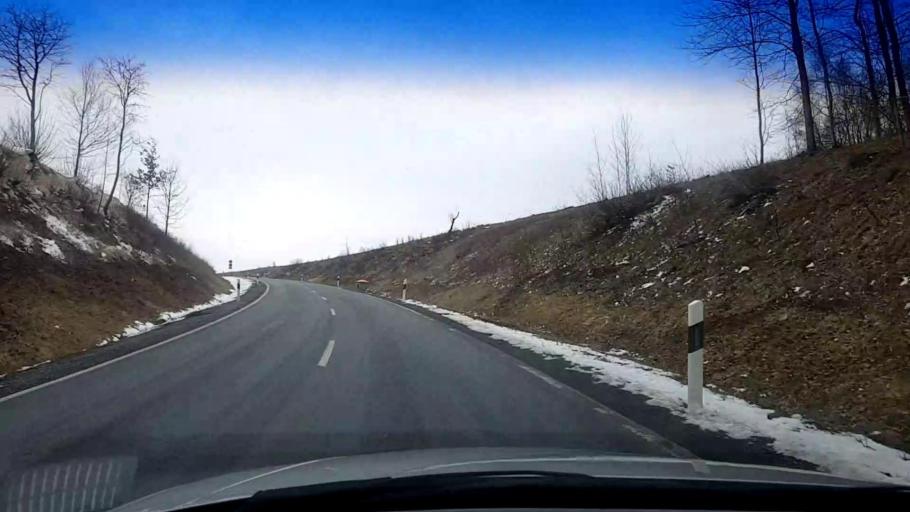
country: DE
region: Bavaria
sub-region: Upper Franconia
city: Gefrees
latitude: 50.0910
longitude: 11.7436
